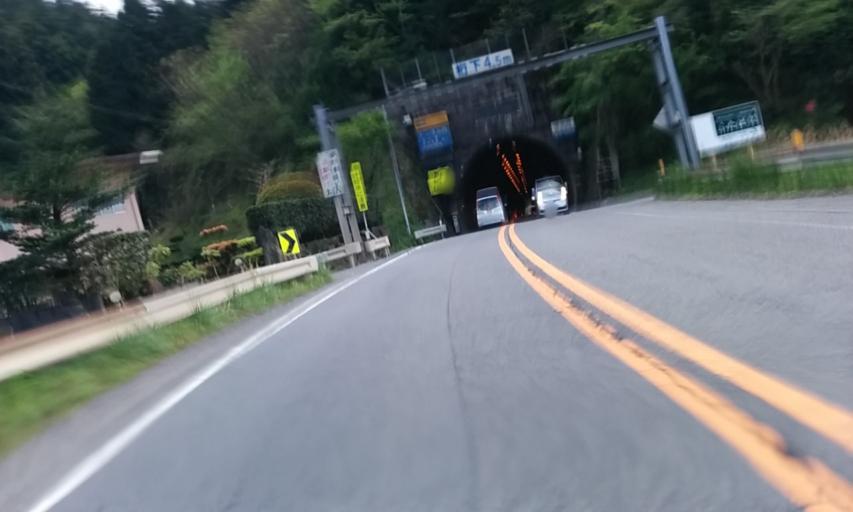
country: JP
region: Ehime
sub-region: Shikoku-chuo Shi
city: Matsuyama
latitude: 33.7986
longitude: 132.9658
